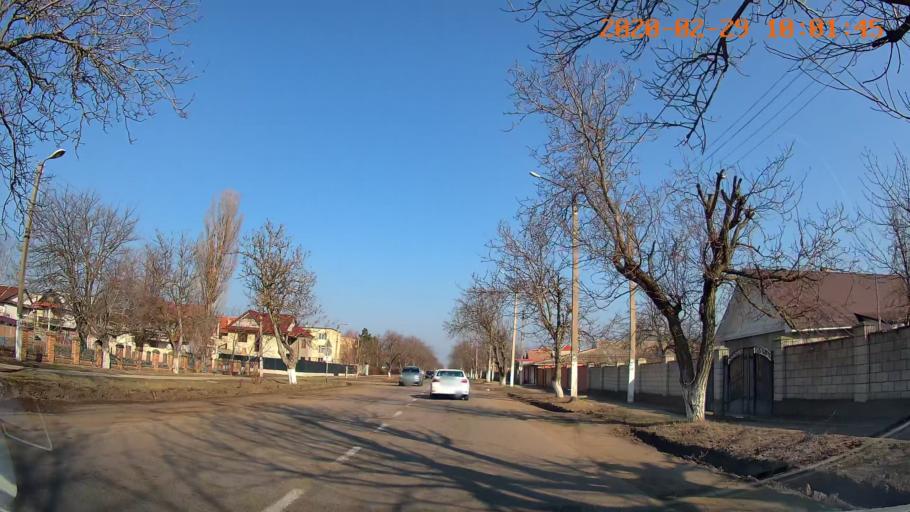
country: MD
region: Telenesti
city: Slobozia
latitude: 46.7775
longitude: 29.6843
